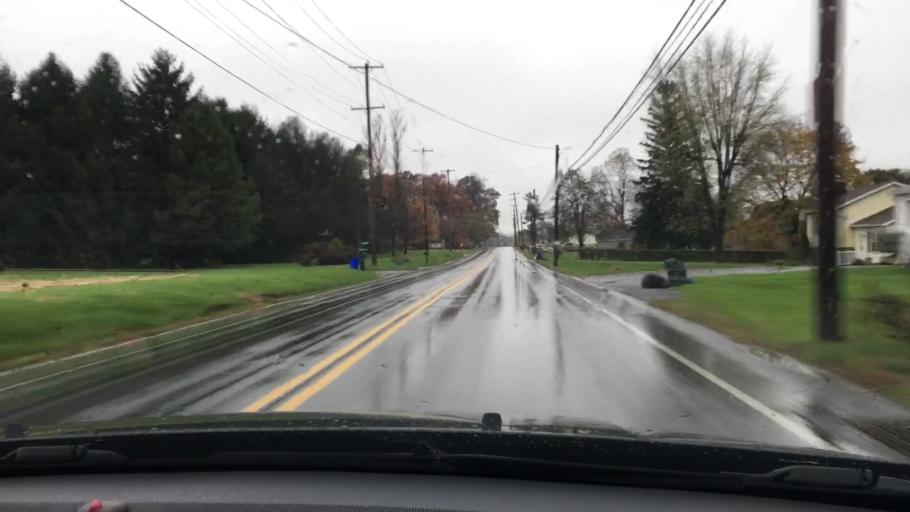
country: US
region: Pennsylvania
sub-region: York County
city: Susquehanna Trails
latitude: 39.8072
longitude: -76.3725
